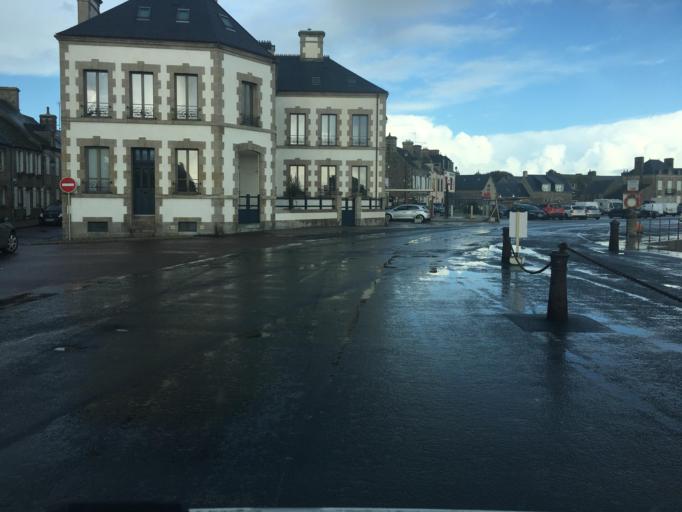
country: FR
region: Lower Normandy
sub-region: Departement de la Manche
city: Reville
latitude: 49.6709
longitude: -1.2634
